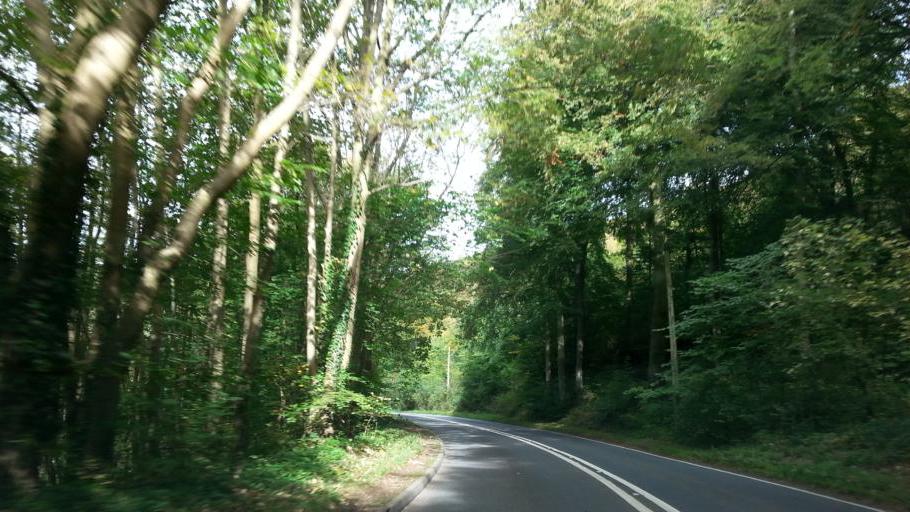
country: GB
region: England
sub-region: Gloucestershire
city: Painswick
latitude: 51.8190
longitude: -2.1688
